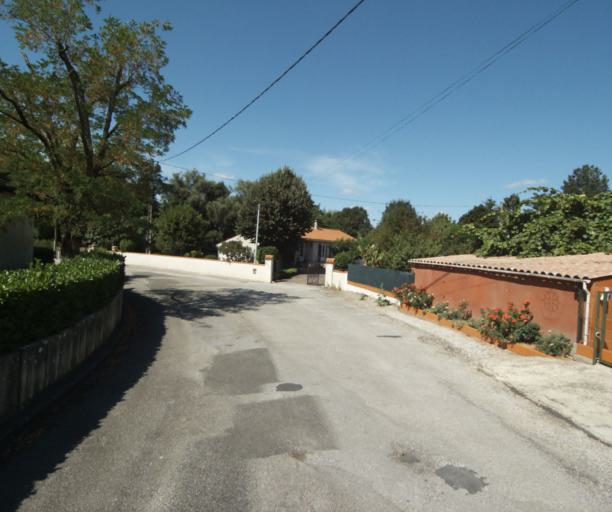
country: FR
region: Midi-Pyrenees
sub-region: Departement de la Haute-Garonne
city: Revel
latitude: 43.4739
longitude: 1.9932
